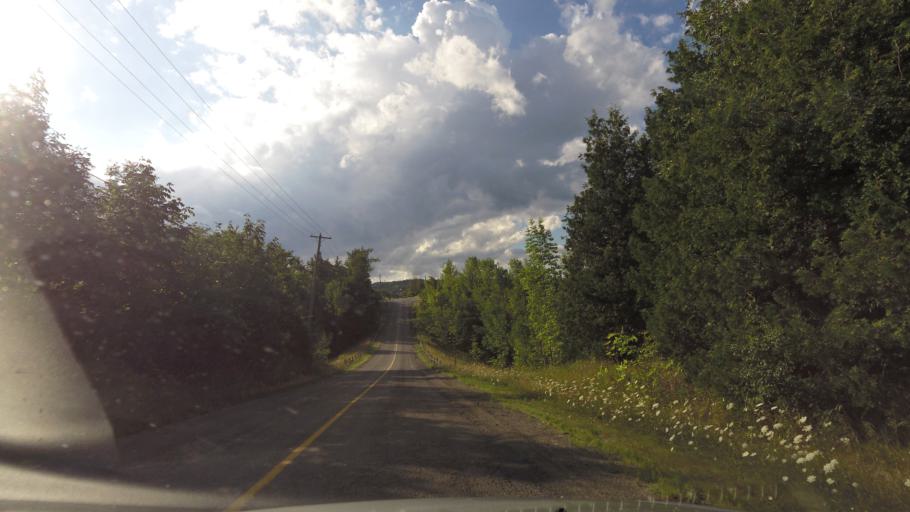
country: CA
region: Ontario
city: Brampton
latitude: 43.7626
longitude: -79.9358
